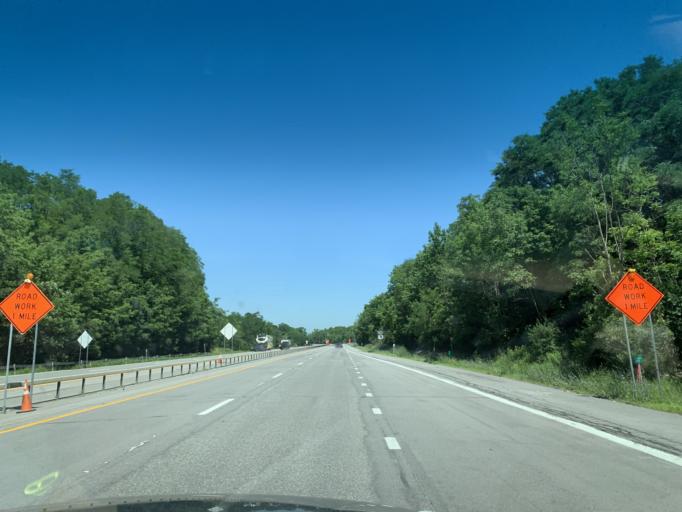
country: US
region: New York
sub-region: Oneida County
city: Chadwicks
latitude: 43.0105
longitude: -75.2544
